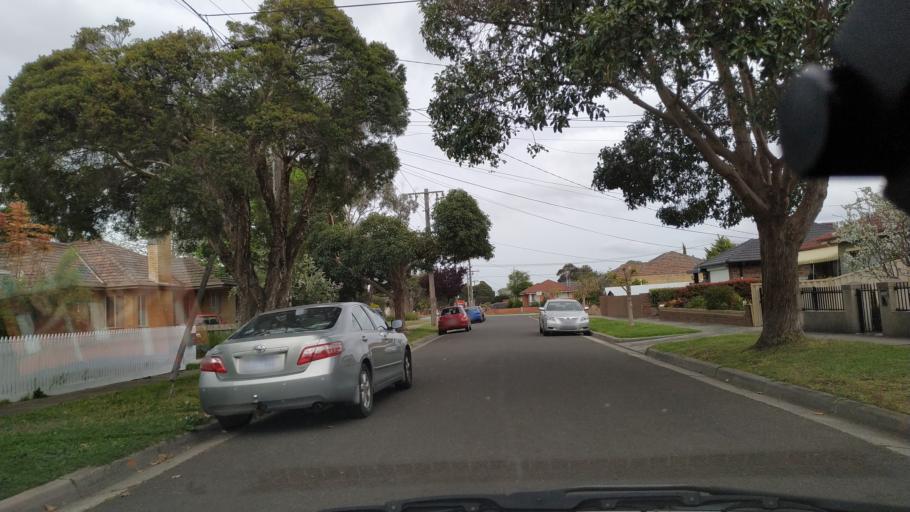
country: AU
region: Victoria
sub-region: Greater Dandenong
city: Dandenong North
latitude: -37.9678
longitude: 145.2036
